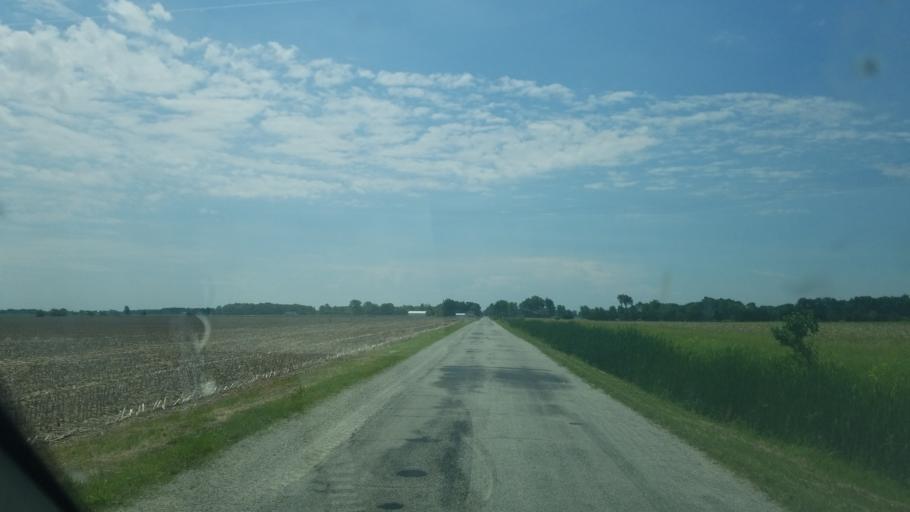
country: US
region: Ohio
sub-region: Wood County
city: North Baltimore
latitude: 41.2504
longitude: -83.6212
